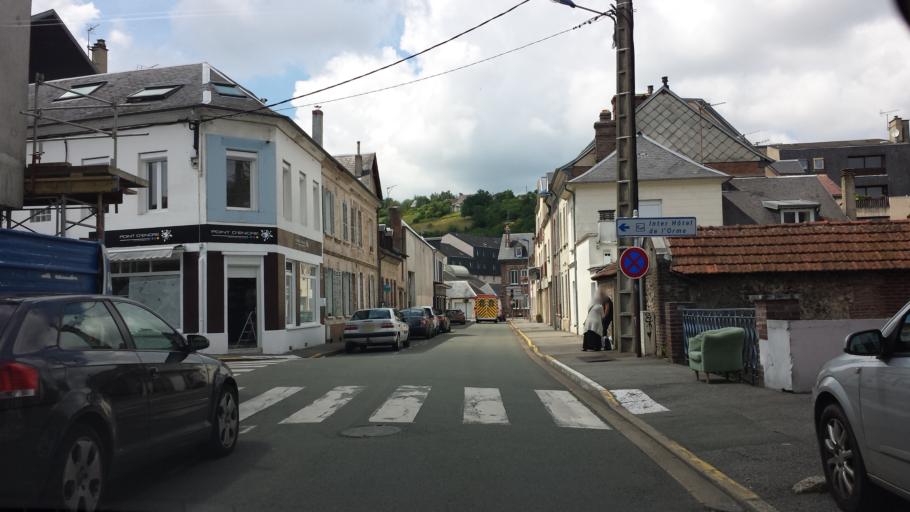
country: FR
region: Haute-Normandie
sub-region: Departement de l'Eure
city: Evreux
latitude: 49.0288
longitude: 1.1504
